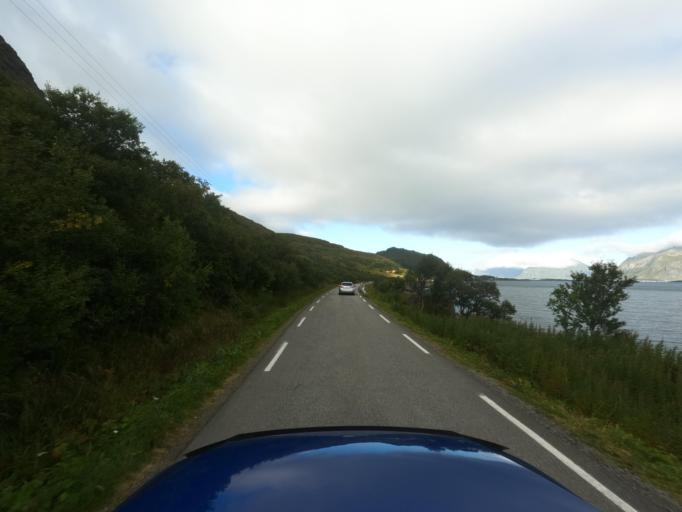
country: NO
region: Nordland
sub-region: Flakstad
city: Ramberg
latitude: 68.0634
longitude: 13.1243
